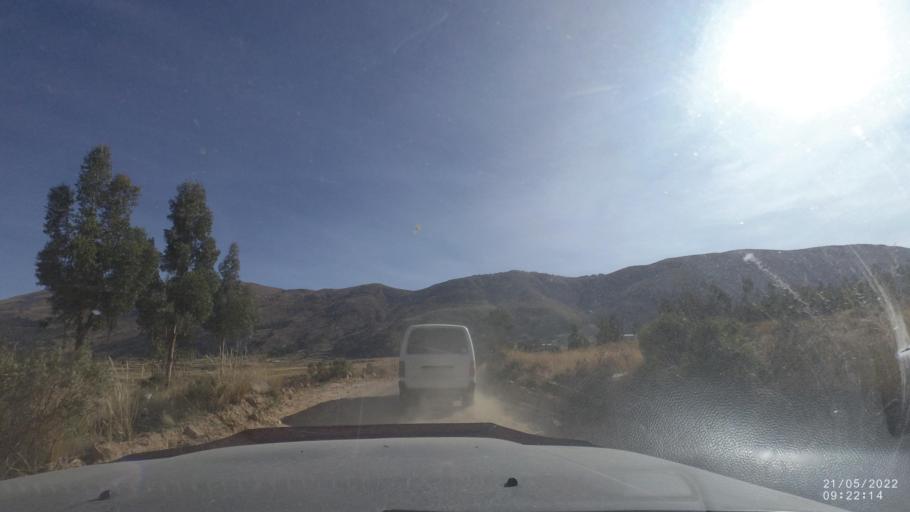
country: BO
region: Cochabamba
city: Cochabamba
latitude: -17.3498
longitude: -66.0145
